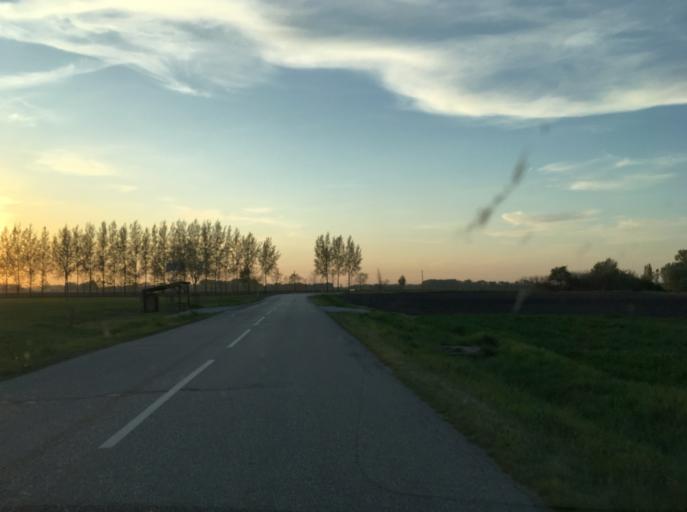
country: SK
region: Nitriansky
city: Kolarovo
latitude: 47.8918
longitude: 17.9233
